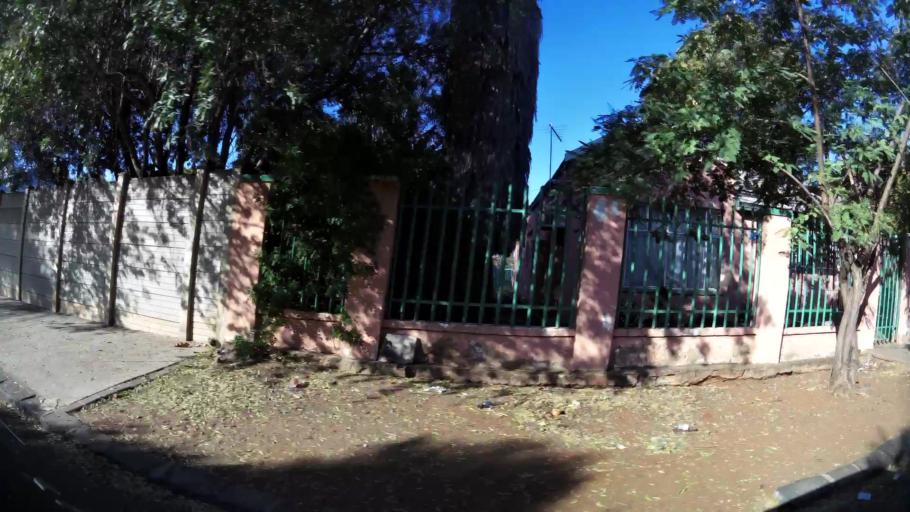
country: ZA
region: Northern Cape
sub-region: Frances Baard District Municipality
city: Kimberley
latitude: -28.7468
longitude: 24.7617
